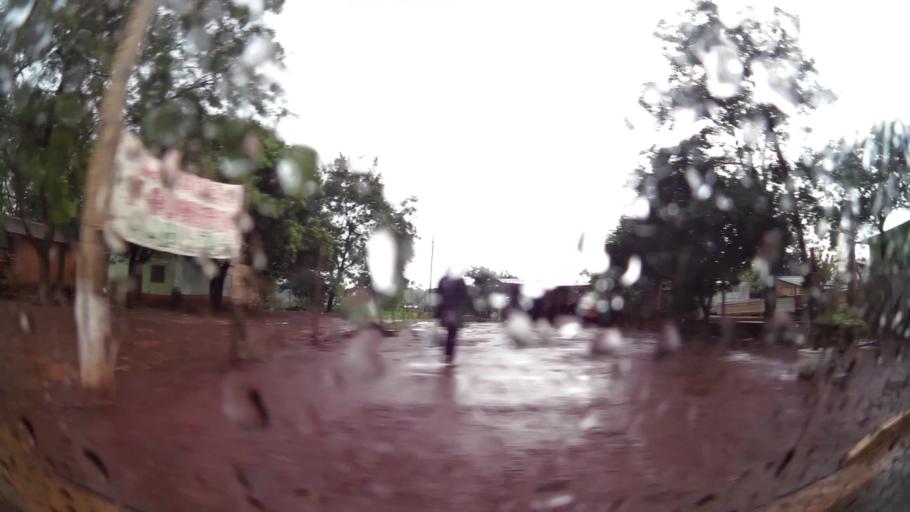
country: PY
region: Alto Parana
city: Presidente Franco
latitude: -25.5481
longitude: -54.6734
